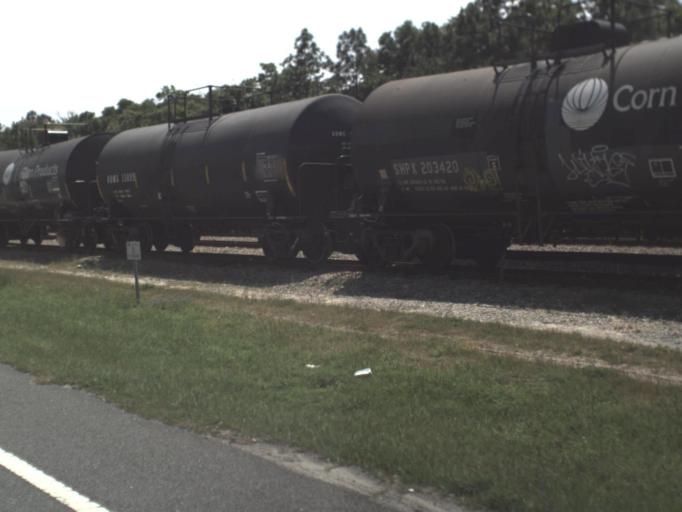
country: US
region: Florida
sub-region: Duval County
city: Jacksonville
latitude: 30.4532
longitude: -81.6374
